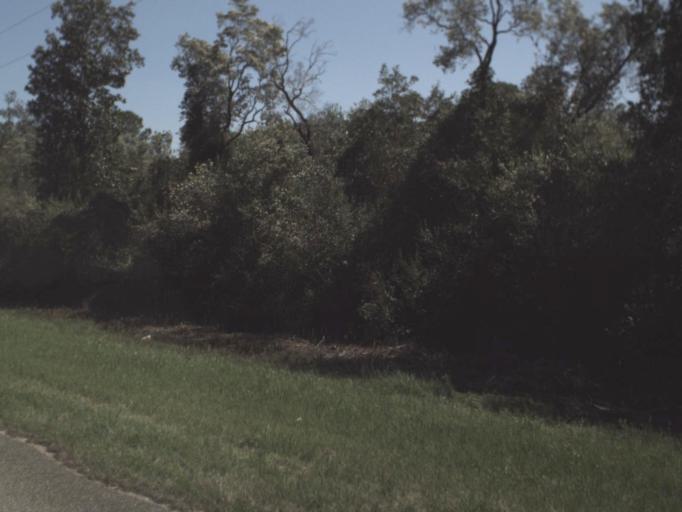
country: US
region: Florida
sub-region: Liberty County
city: Bristol
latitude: 30.4131
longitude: -84.8572
